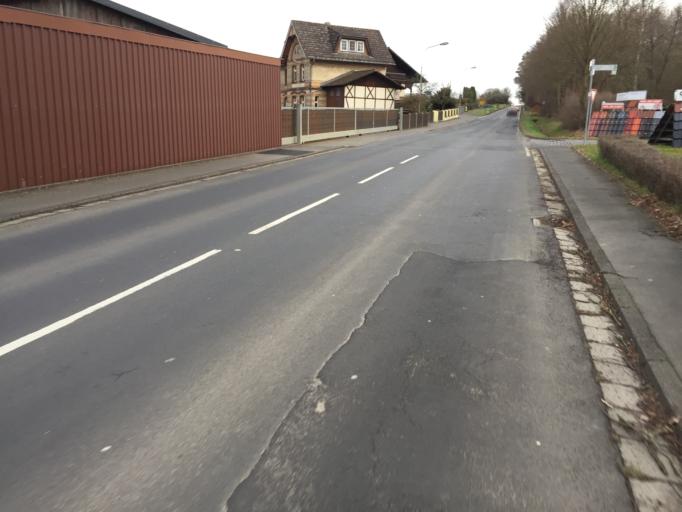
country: DE
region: Hesse
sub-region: Regierungsbezirk Giessen
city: Rabenau
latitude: 50.6668
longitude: 8.8745
